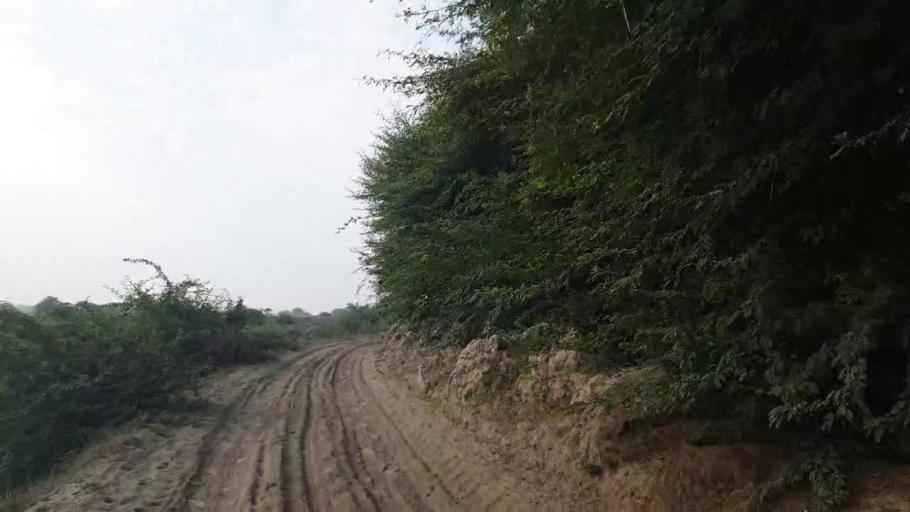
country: PK
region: Sindh
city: Tando Bago
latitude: 24.7837
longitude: 68.8797
